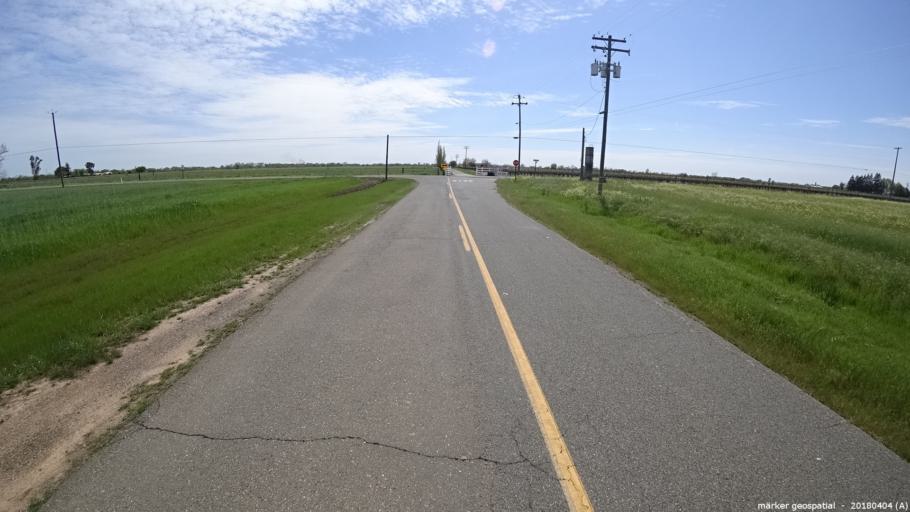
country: US
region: California
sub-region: Sacramento County
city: Herald
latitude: 38.2637
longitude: -121.2082
